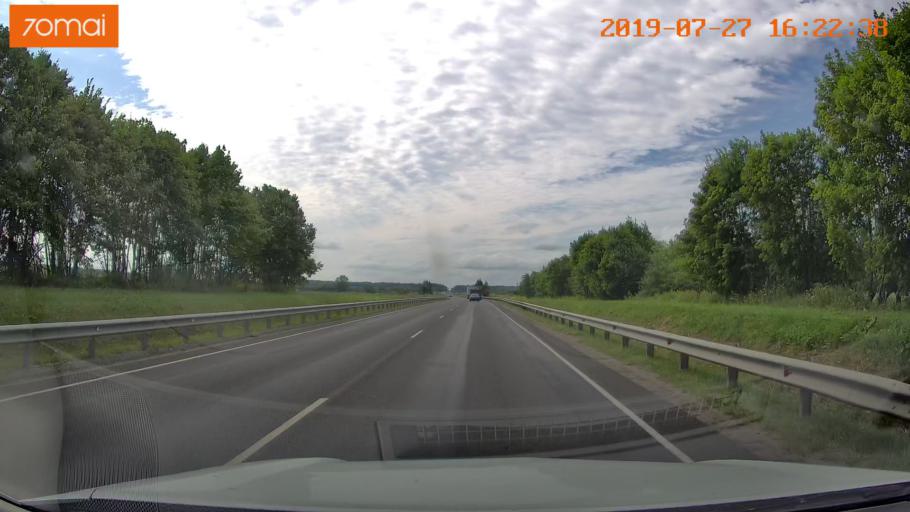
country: RU
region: Kaliningrad
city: Chernyakhovsk
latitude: 54.6287
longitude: 21.4909
